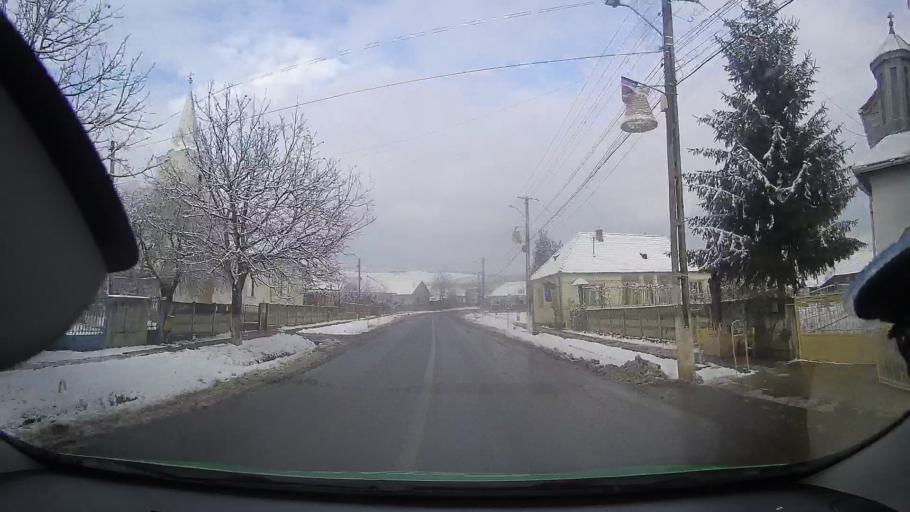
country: RO
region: Mures
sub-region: Comuna Atintis
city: Atintis
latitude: 46.4292
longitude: 24.1048
